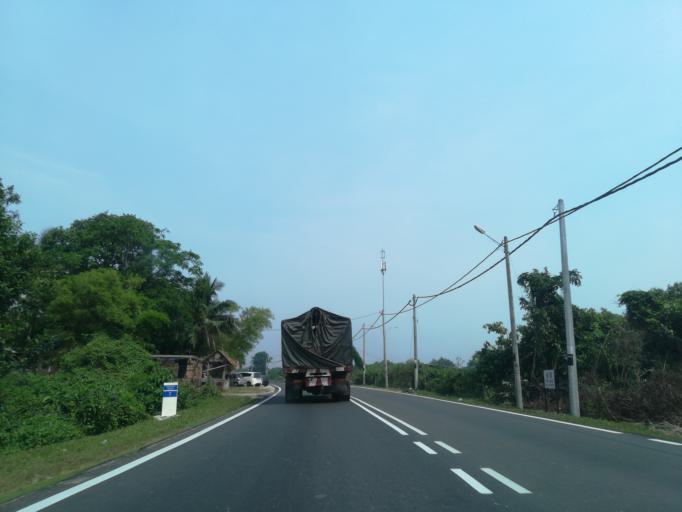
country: MY
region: Penang
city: Tasek Glugor
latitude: 5.4630
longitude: 100.5458
